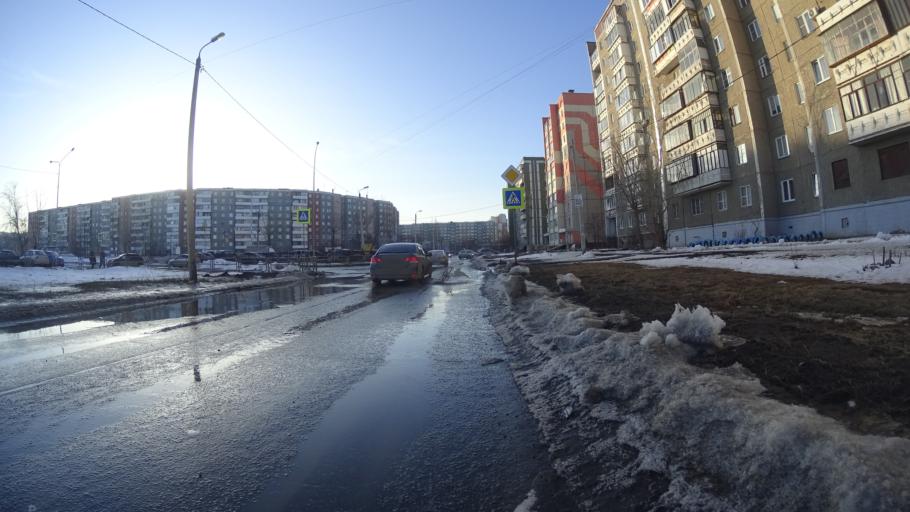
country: RU
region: Chelyabinsk
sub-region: Gorod Chelyabinsk
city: Chelyabinsk
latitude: 55.1360
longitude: 61.4530
